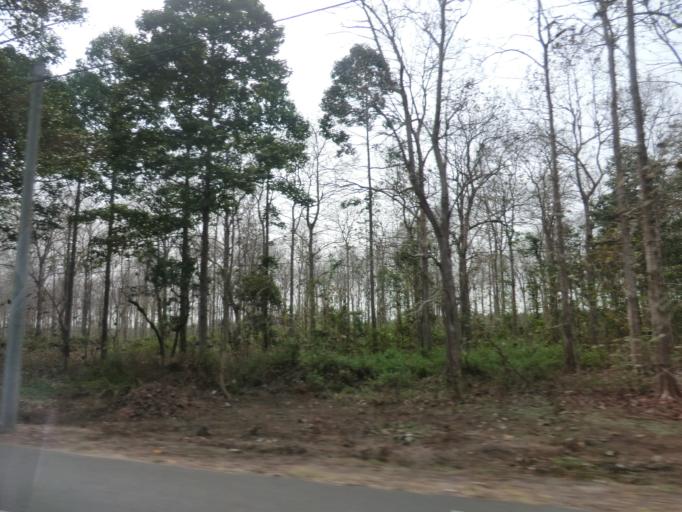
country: VN
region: Dong Nai
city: Tan Phu
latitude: 11.2515
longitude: 107.4070
